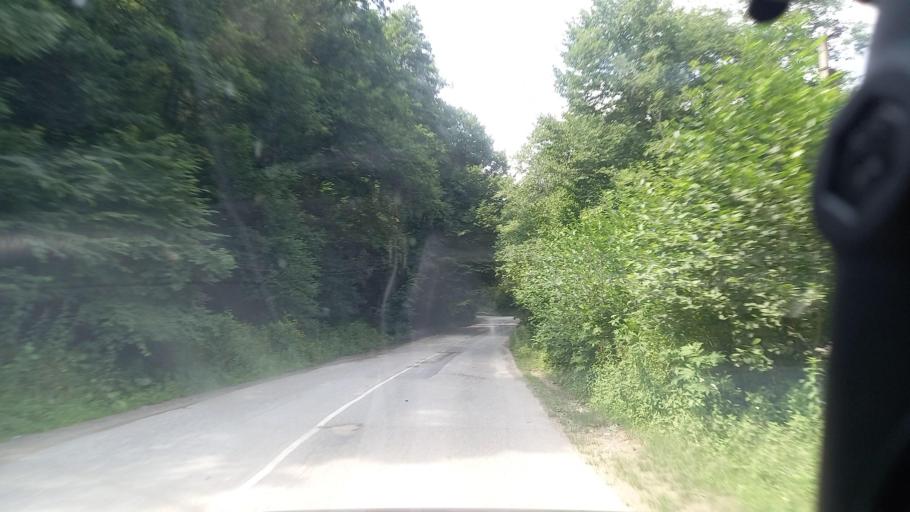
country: RU
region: Karachayevo-Cherkesiya
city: Kurdzhinovo
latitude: 43.9753
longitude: 40.9649
